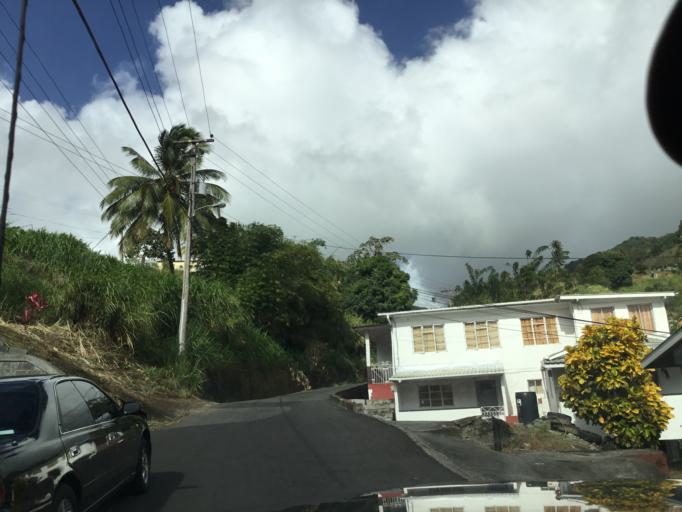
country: VC
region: Saint George
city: Kingstown
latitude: 13.1704
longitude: -61.2198
